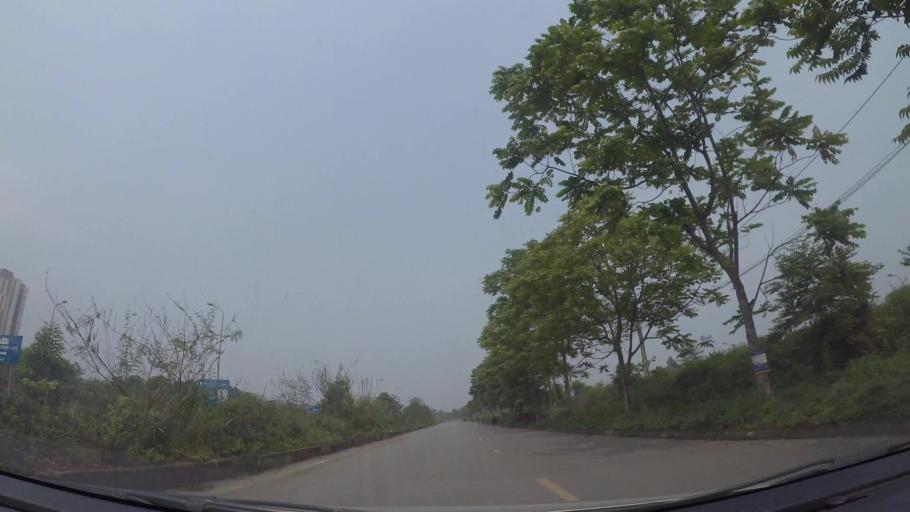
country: VN
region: Ha Noi
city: Lien Quan
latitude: 20.9908
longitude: 105.5317
